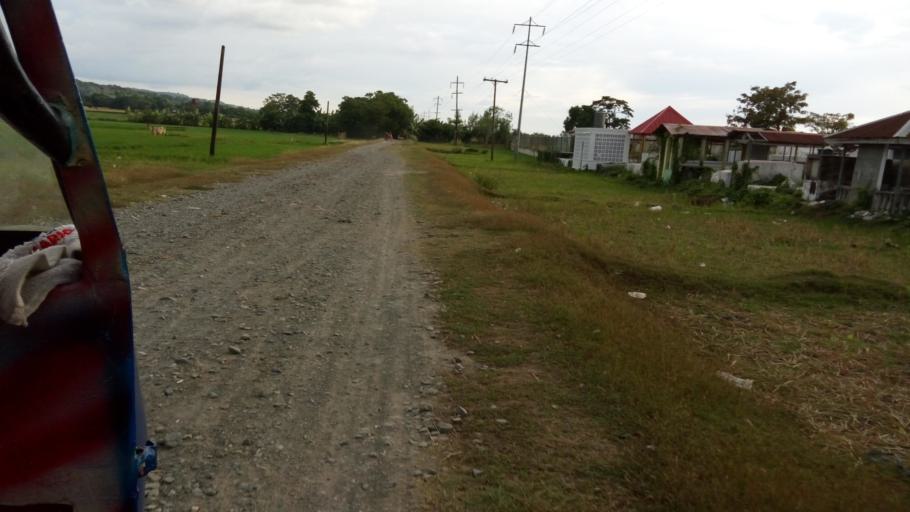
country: PH
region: Ilocos
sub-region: Province of La Union
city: Santo Tomas
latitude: 16.2834
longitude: 120.3840
